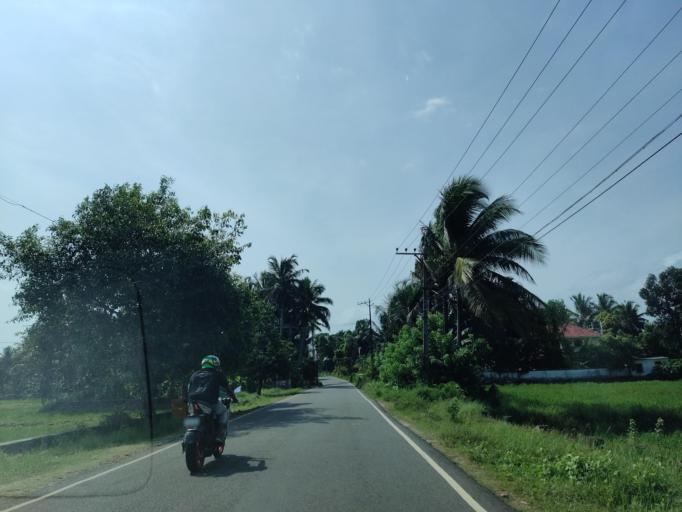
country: IN
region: Kerala
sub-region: Pattanamtitta
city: Tiruvalla
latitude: 9.3541
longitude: 76.4690
